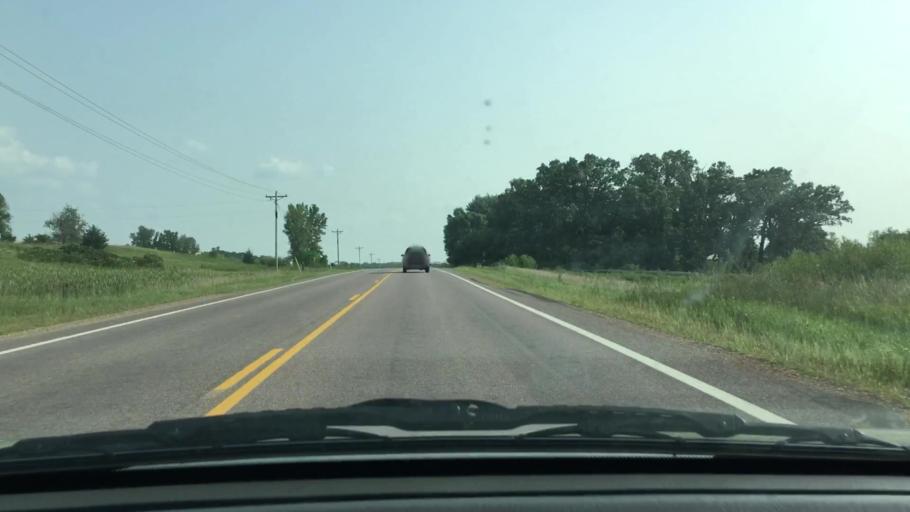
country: US
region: Minnesota
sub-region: Scott County
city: Elko New Market
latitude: 44.5522
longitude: -93.3393
